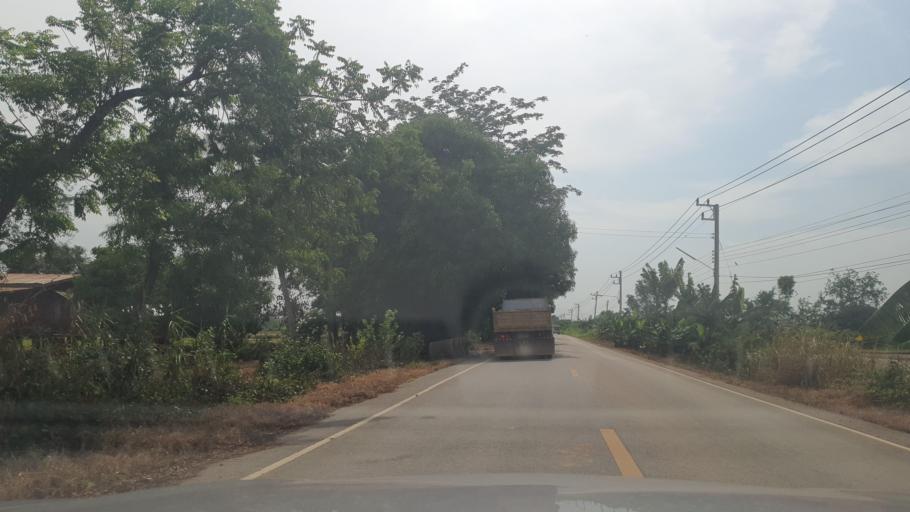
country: TH
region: Sukhothai
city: Si Samrong
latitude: 17.1174
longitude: 99.8751
